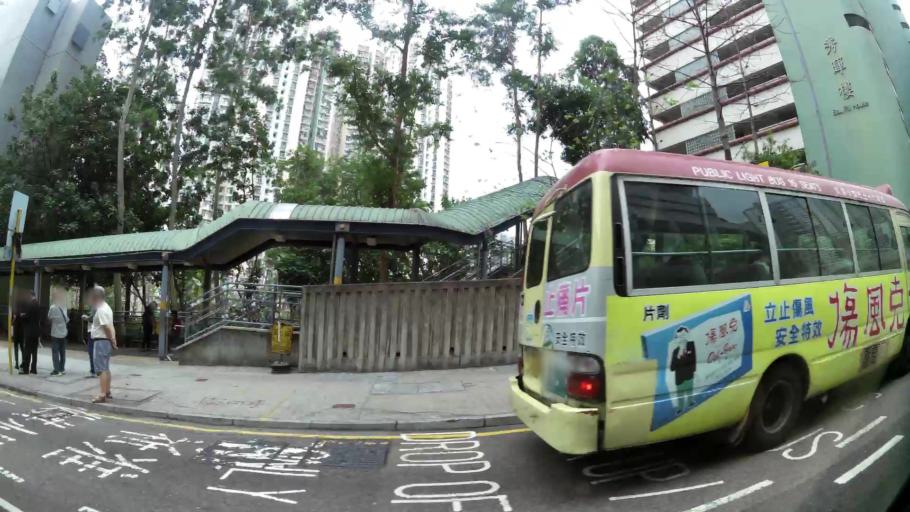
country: HK
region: Kowloon City
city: Kowloon
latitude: 22.3173
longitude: 114.2355
